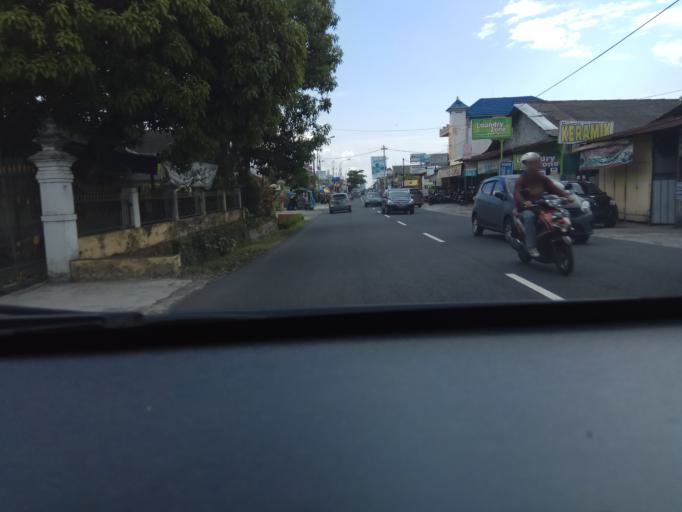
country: ID
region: Daerah Istimewa Yogyakarta
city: Melati
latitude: -7.7175
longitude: 110.4052
